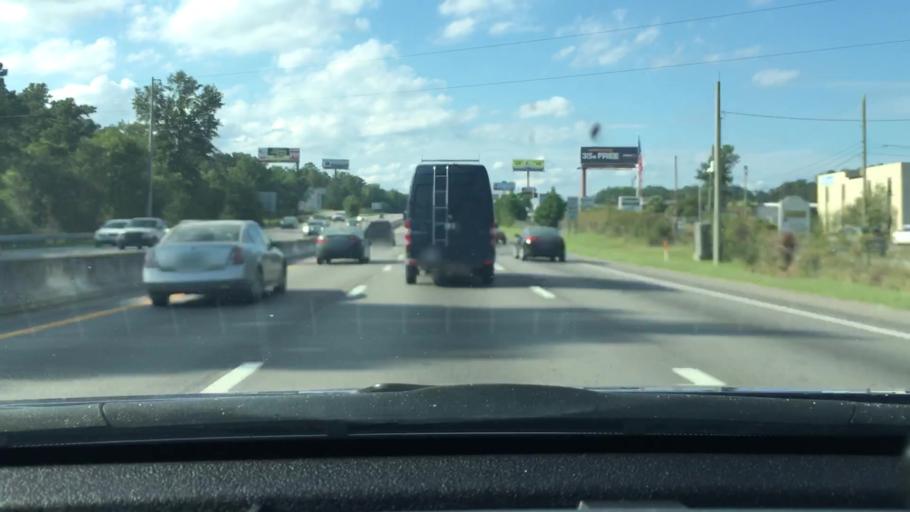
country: US
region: South Carolina
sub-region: Lexington County
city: Saint Andrews
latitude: 34.0507
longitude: -81.1243
